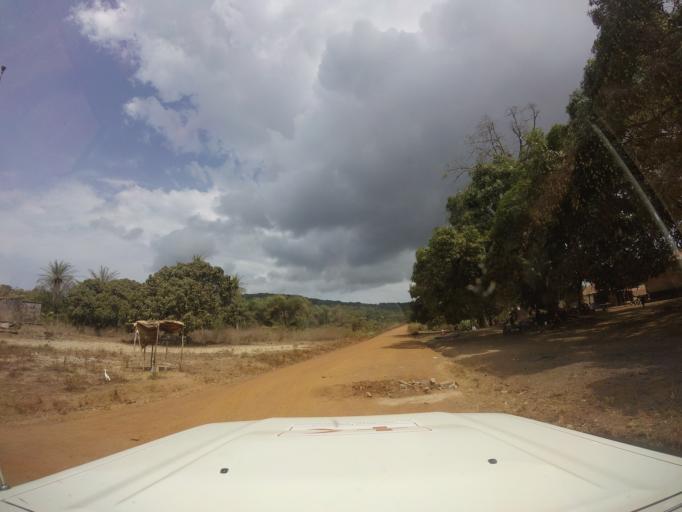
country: LR
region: Grand Cape Mount
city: Robertsport
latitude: 6.7073
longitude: -11.3340
